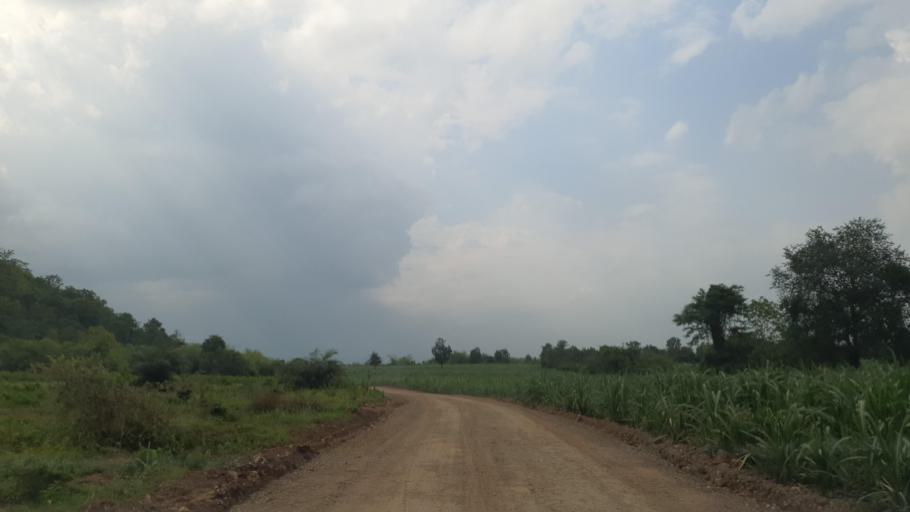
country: TH
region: Sukhothai
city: Thung Saliam
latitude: 17.2534
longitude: 99.5425
